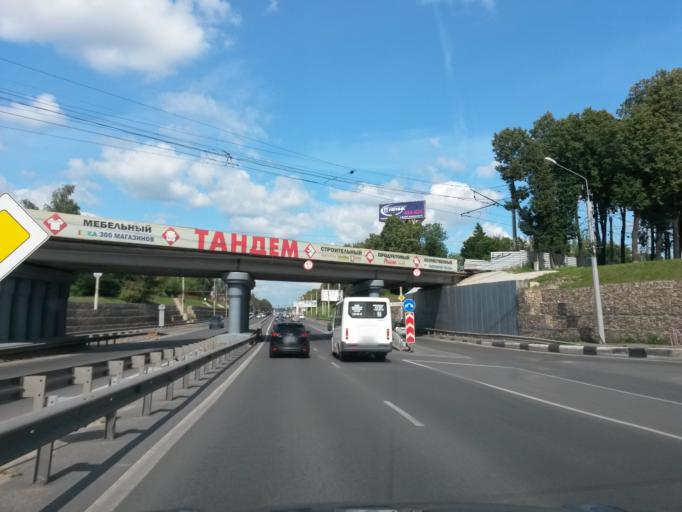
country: RU
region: Jaroslavl
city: Yaroslavl
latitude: 57.6017
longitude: 39.8768
